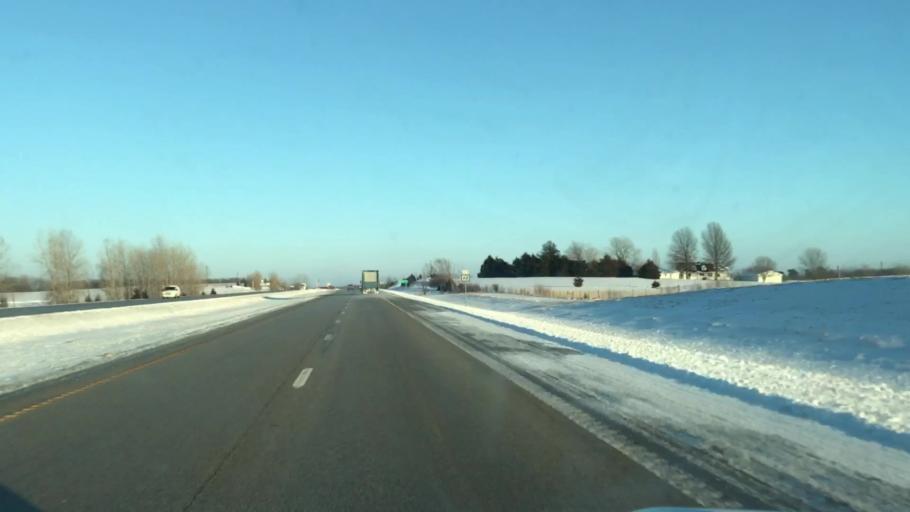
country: US
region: Missouri
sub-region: Clinton County
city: Gower
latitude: 39.7470
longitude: -94.6169
